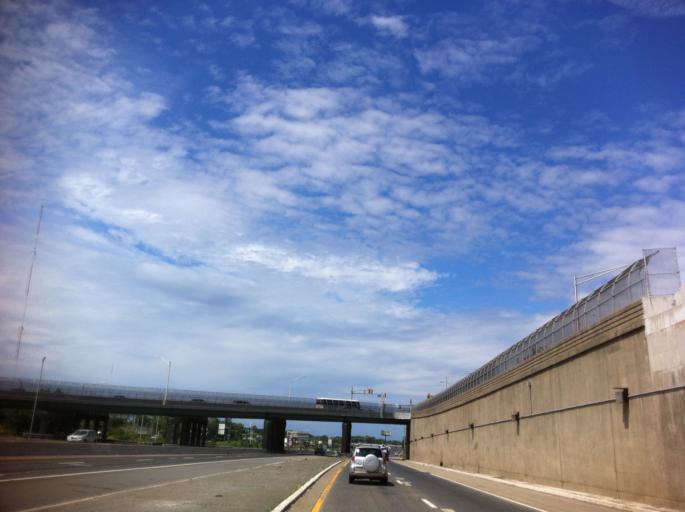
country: US
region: New Jersey
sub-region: Bergen County
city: Hackensack
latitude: 40.8715
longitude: -74.0586
